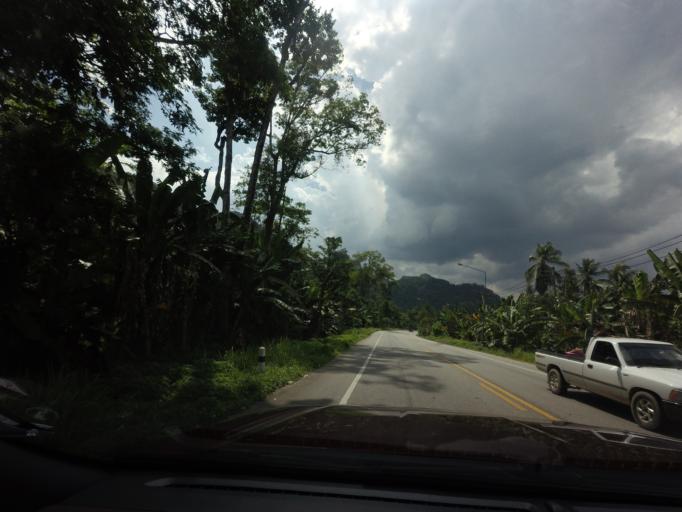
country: TH
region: Yala
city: Than To
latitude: 6.1864
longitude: 101.1736
